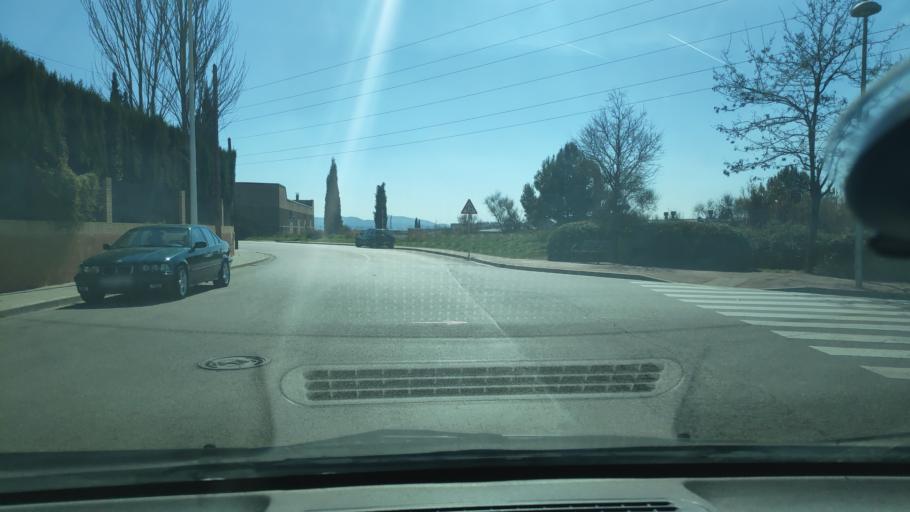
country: ES
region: Catalonia
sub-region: Provincia de Barcelona
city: Rubi
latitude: 41.5064
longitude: 2.0447
